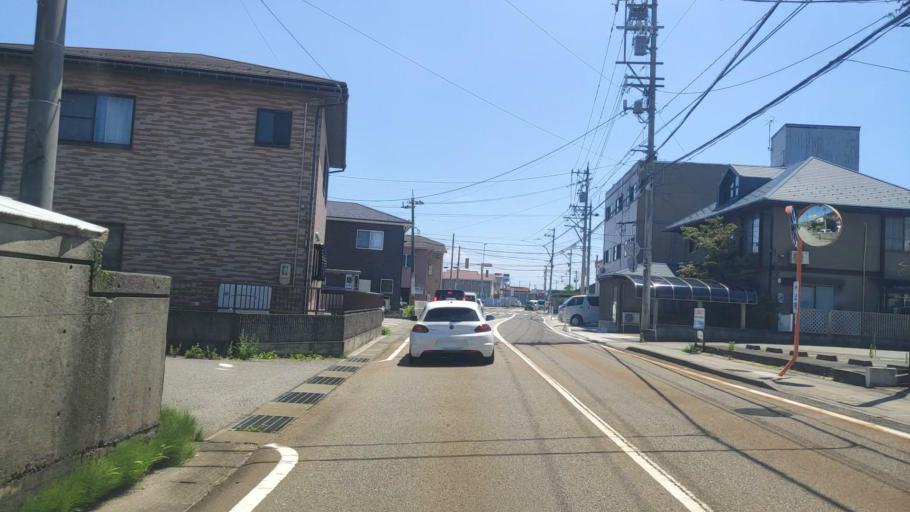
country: JP
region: Ishikawa
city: Kanazawa-shi
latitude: 36.6411
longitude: 136.6421
